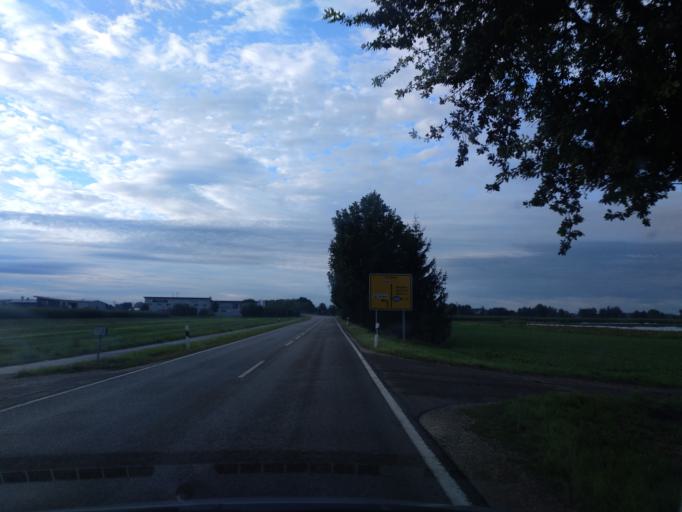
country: DE
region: Bavaria
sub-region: Upper Bavaria
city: Burgheim
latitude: 48.7145
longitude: 11.0068
